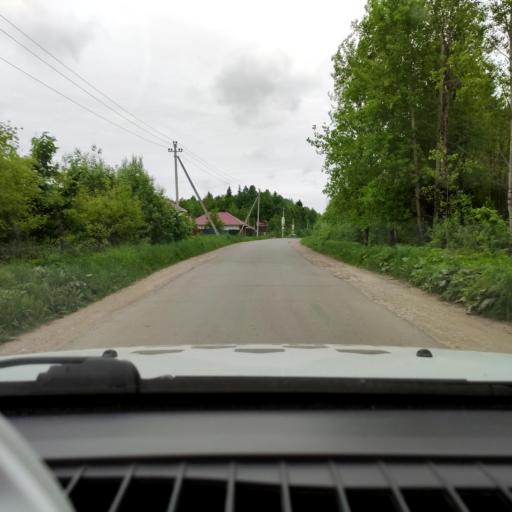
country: RU
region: Perm
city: Novyye Lyady
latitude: 58.0439
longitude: 56.6172
